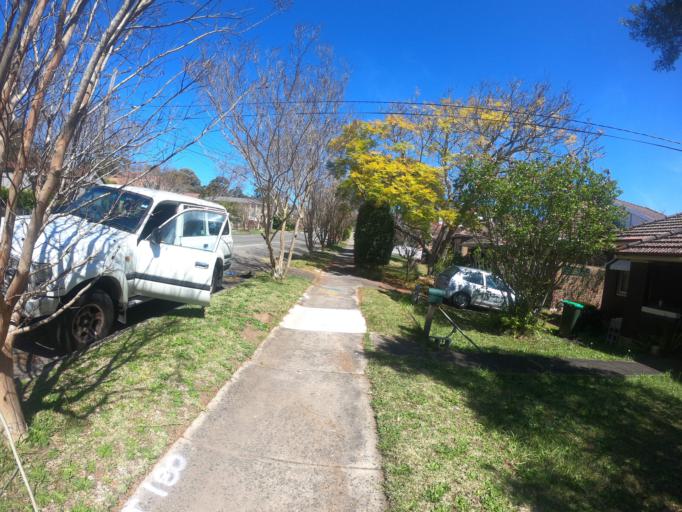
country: AU
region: New South Wales
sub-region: Ryde
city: East Ryde
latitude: -33.8200
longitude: 151.1274
